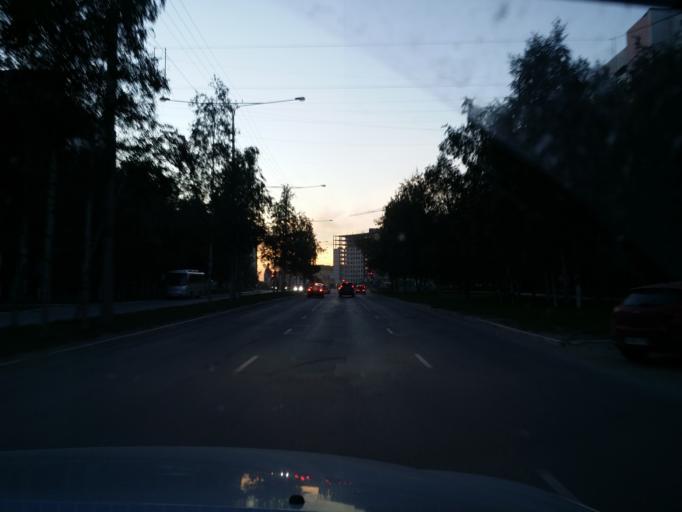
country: RU
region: Khanty-Mansiyskiy Avtonomnyy Okrug
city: Nizhnevartovsk
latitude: 60.9441
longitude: 76.5664
